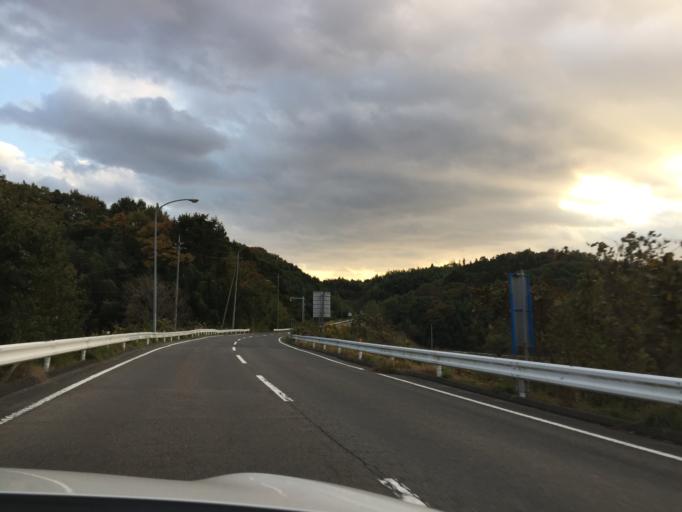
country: JP
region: Fukushima
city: Miharu
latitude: 37.4399
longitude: 140.4395
